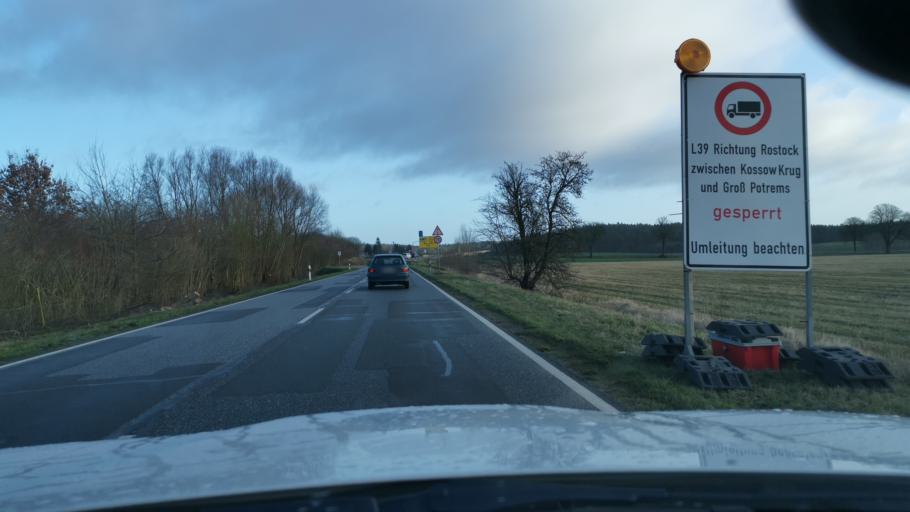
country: DE
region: Mecklenburg-Vorpommern
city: Laage
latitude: 53.9355
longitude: 12.3144
